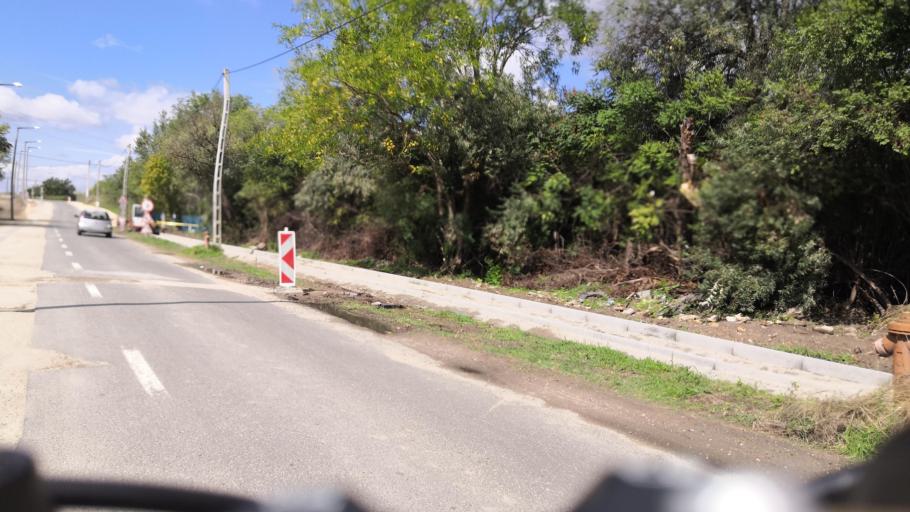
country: HU
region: Csongrad
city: Szeged
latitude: 46.2762
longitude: 20.1386
